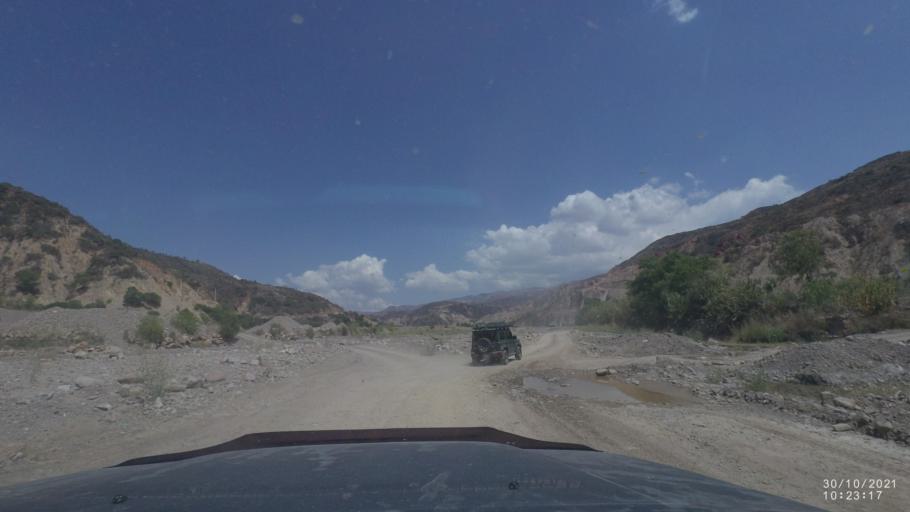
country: BO
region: Cochabamba
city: Sipe Sipe
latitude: -17.5571
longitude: -66.3862
